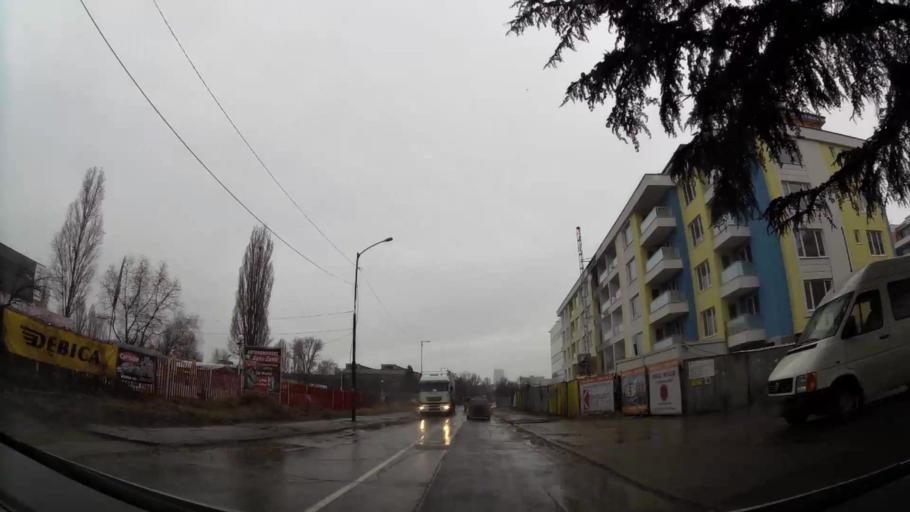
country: BG
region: Sofia-Capital
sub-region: Stolichna Obshtina
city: Sofia
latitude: 42.6635
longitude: 23.4056
